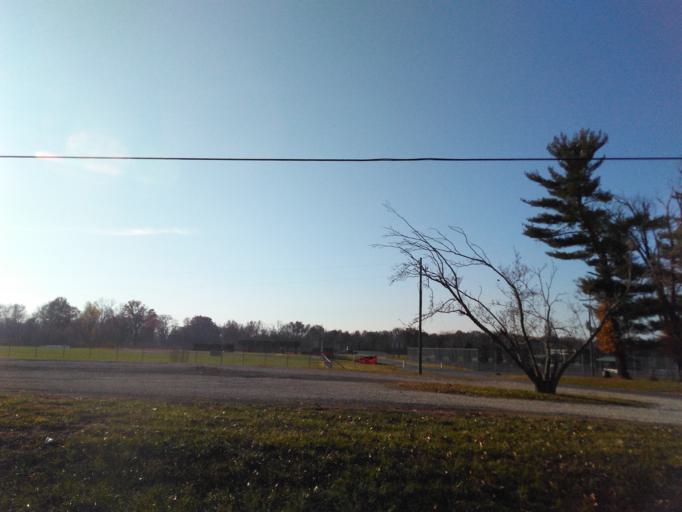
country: US
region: Illinois
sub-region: Madison County
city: Troy
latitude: 38.7176
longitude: -89.8531
